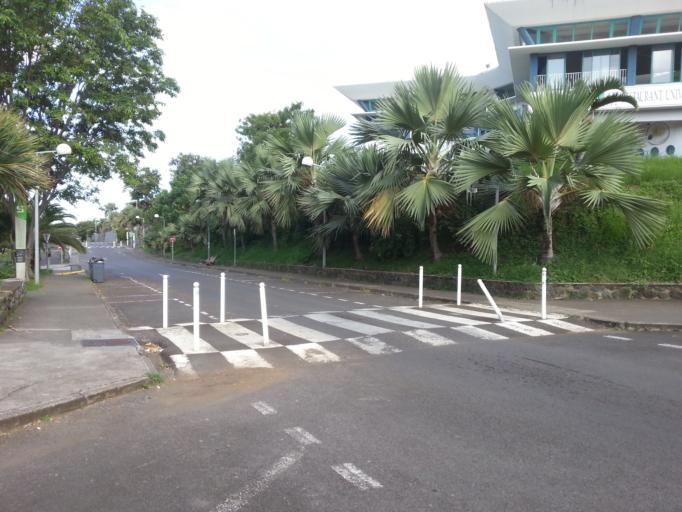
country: RE
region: Reunion
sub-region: Reunion
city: Saint-Denis
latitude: -20.9016
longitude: 55.4836
